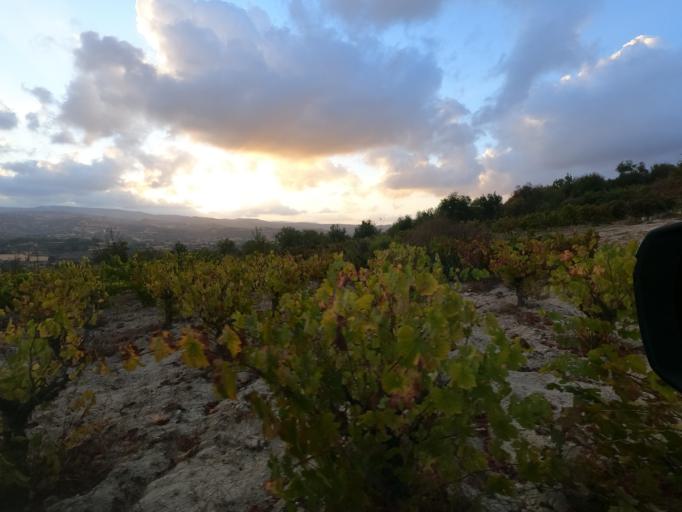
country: CY
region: Pafos
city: Mesogi
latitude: 34.8473
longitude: 32.5342
